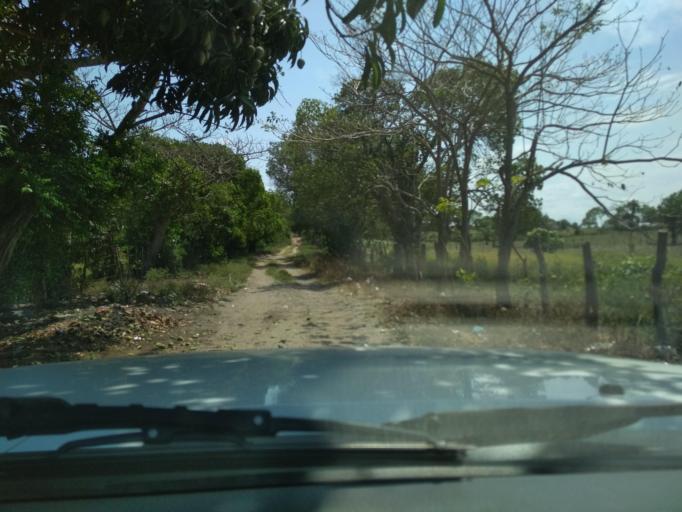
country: MX
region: Veracruz
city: Anton Lizardo
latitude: 19.0013
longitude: -95.9891
